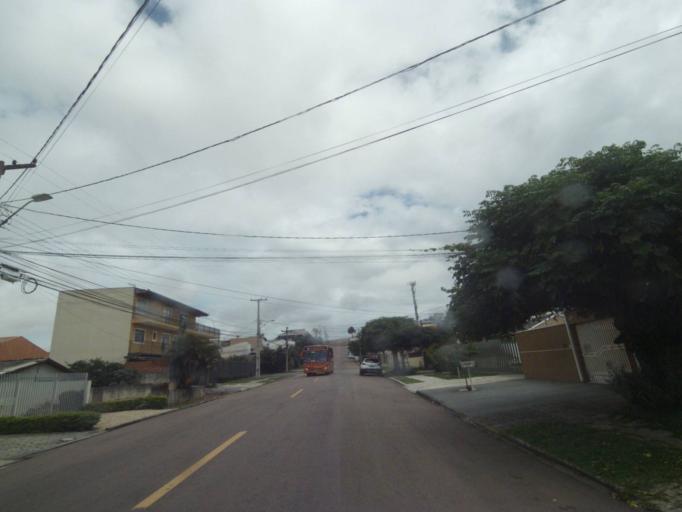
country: BR
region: Parana
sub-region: Curitiba
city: Curitiba
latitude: -25.4800
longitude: -49.2815
